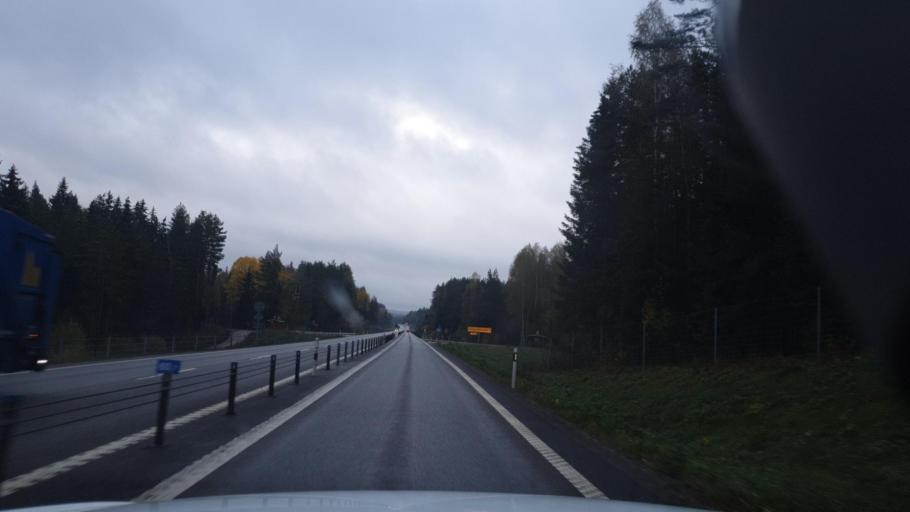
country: SE
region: Vaermland
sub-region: Arvika Kommun
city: Arvika
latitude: 59.6473
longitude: 12.7086
